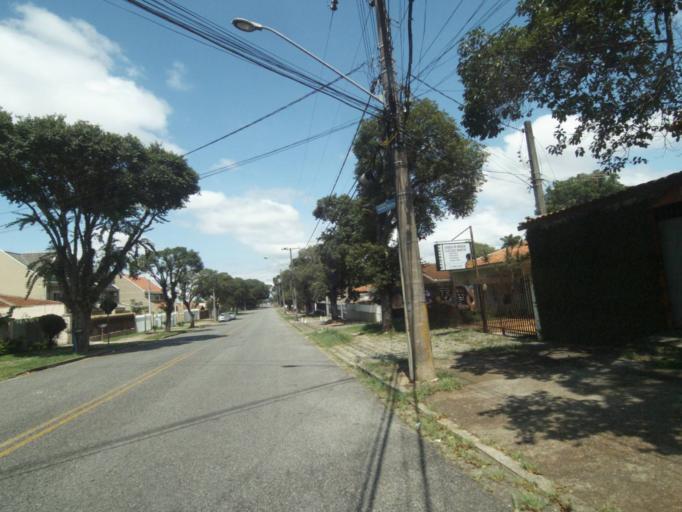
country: BR
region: Parana
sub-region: Pinhais
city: Pinhais
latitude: -25.4426
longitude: -49.2270
